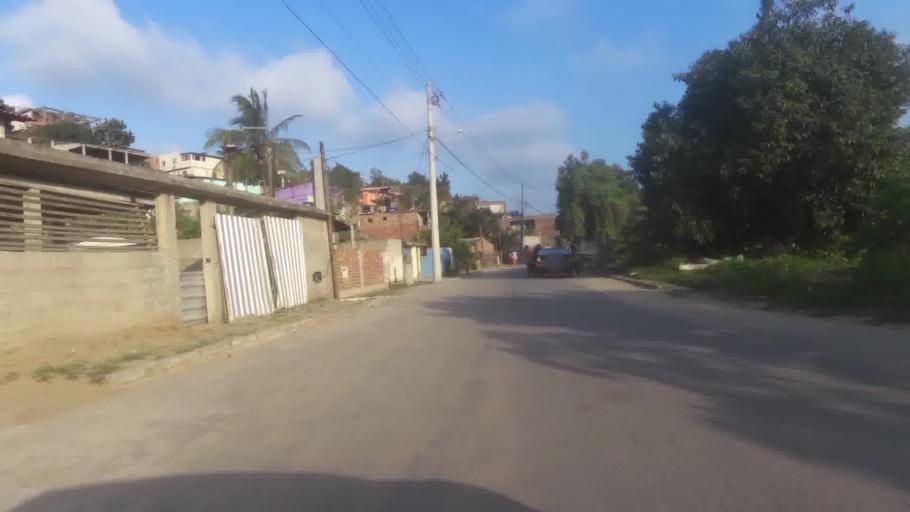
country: BR
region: Espirito Santo
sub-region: Itapemirim
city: Itapemirim
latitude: -21.0145
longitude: -40.8307
